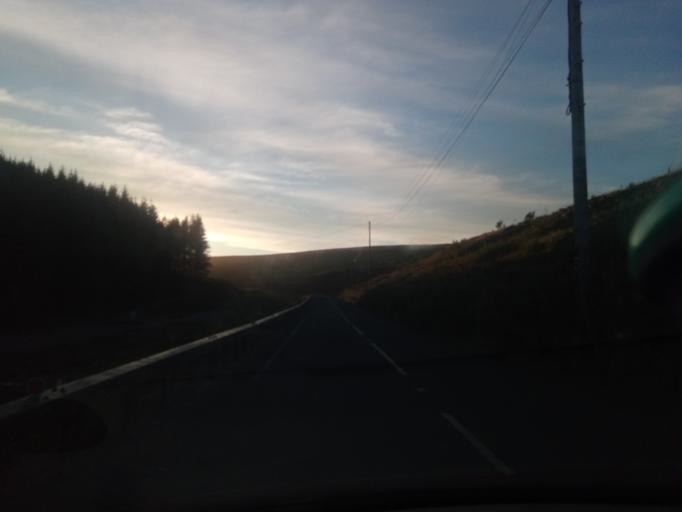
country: GB
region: England
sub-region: County Durham
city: Holwick
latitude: 54.7830
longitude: -2.2717
